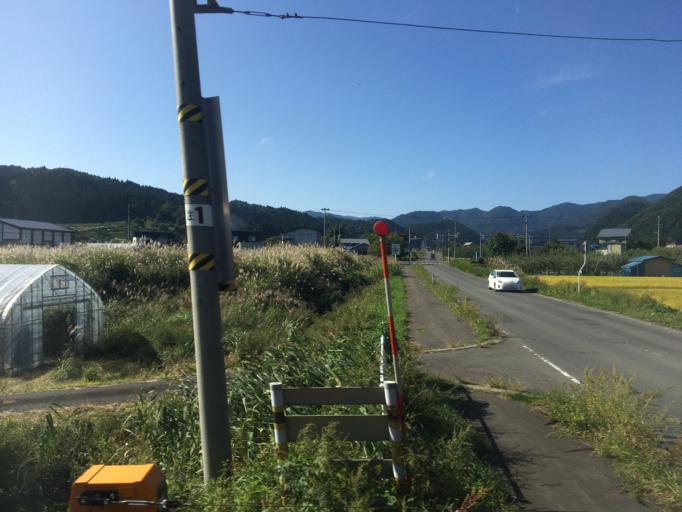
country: JP
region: Aomori
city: Hirosaki
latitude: 40.5248
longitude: 140.5543
